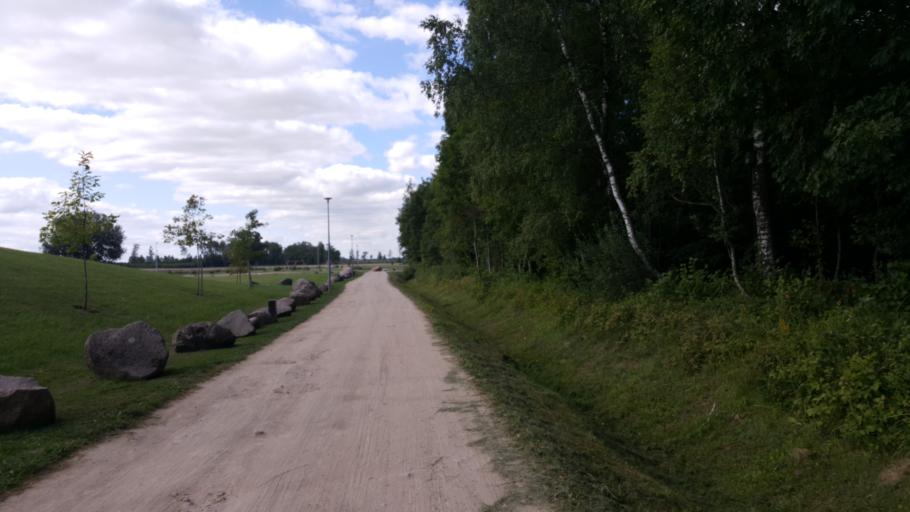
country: LT
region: Siauliu apskritis
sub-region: Siauliai
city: Siauliai
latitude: 56.0216
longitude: 23.5036
